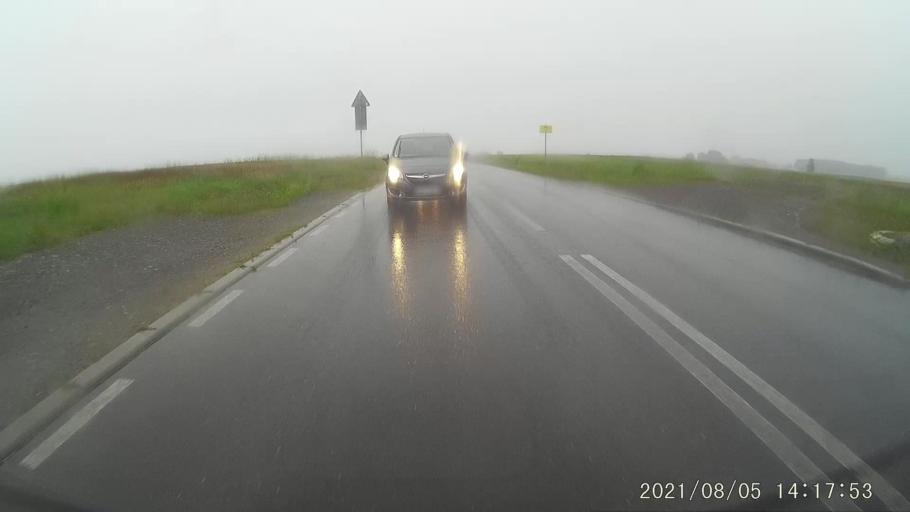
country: PL
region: Opole Voivodeship
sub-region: Powiat prudnicki
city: Biala
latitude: 50.4629
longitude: 17.7000
